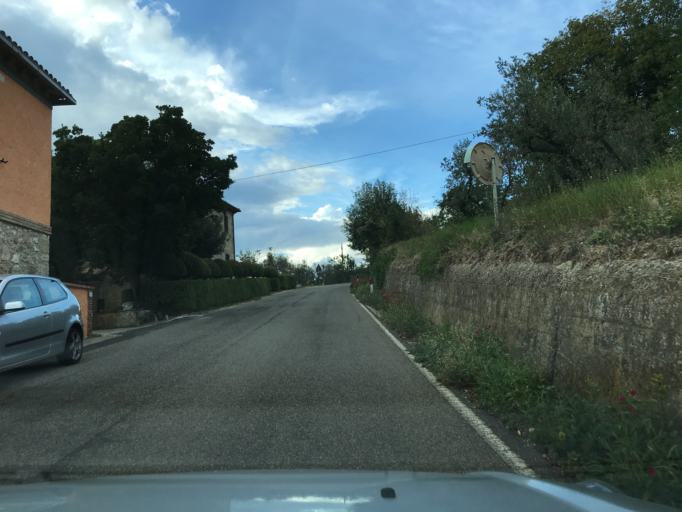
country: IT
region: Umbria
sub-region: Provincia di Terni
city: Montecchio
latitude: 42.6714
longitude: 12.2926
